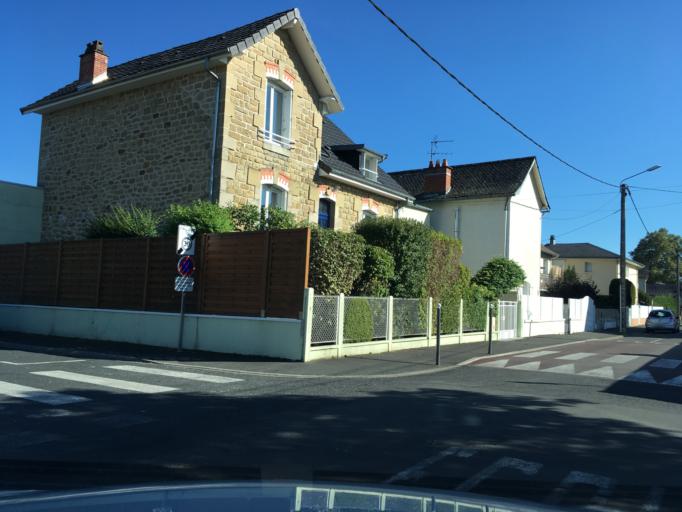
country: FR
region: Limousin
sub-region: Departement de la Correze
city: Brive-la-Gaillarde
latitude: 45.1668
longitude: 1.5385
